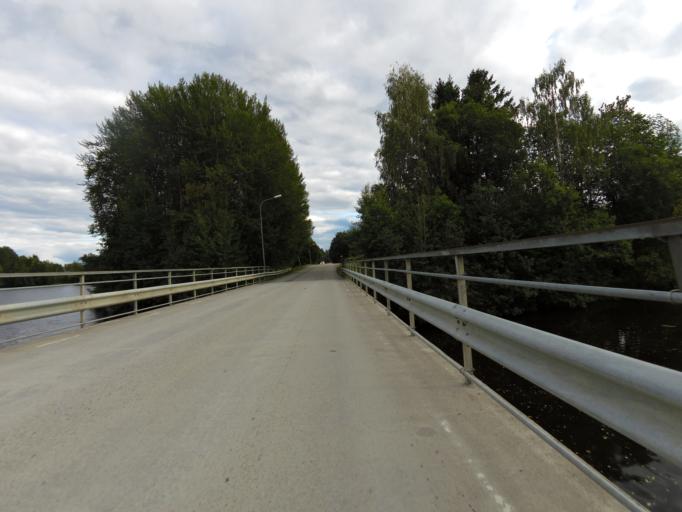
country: SE
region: Gaevleborg
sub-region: Gavle Kommun
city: Valbo
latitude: 60.6526
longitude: 17.0138
